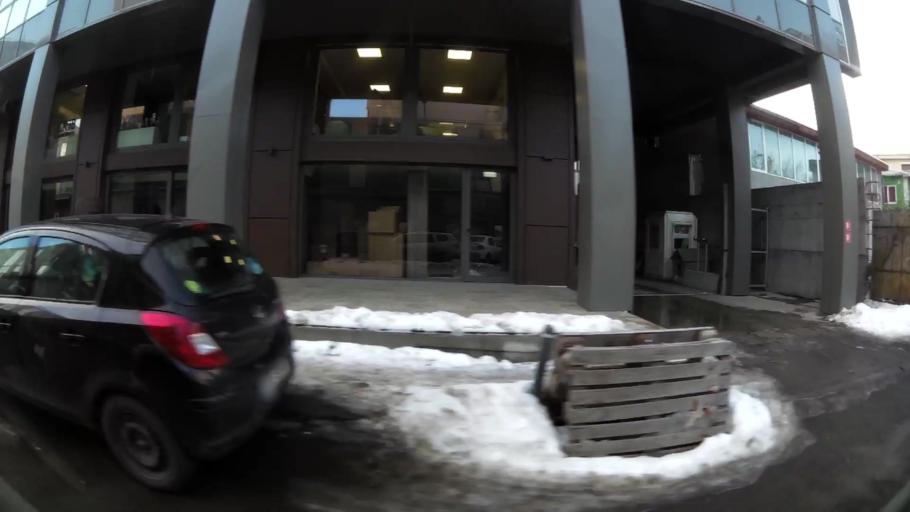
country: RO
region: Bucuresti
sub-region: Municipiul Bucuresti
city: Bucharest
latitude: 44.4234
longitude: 26.1337
